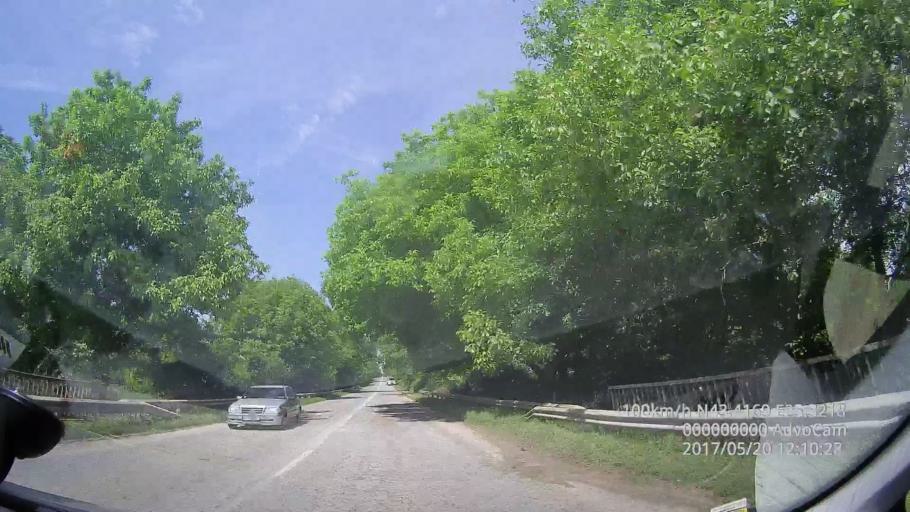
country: BG
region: Veliko Turnovo
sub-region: Obshtina Pavlikeni
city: Pavlikeni
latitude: 43.4169
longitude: 25.3212
